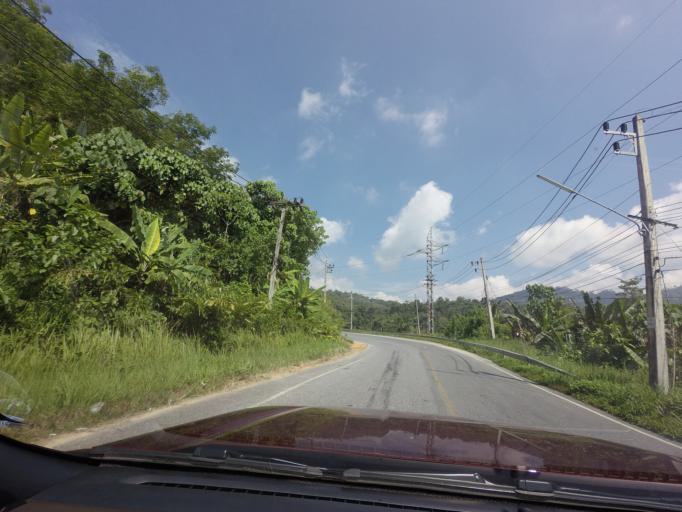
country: TH
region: Yala
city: Betong
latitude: 5.8807
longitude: 101.1384
